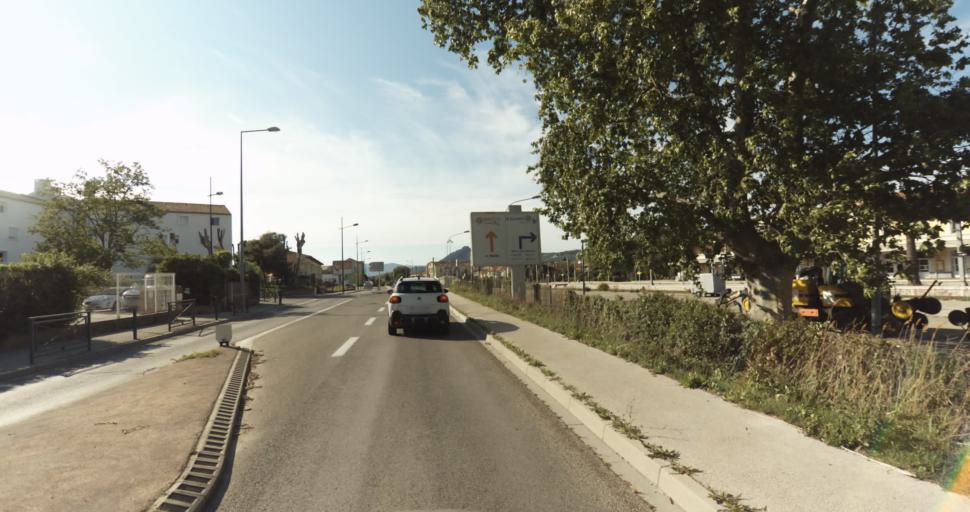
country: FR
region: Provence-Alpes-Cote d'Azur
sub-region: Departement du Var
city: Hyeres
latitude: 43.1082
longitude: 6.1240
